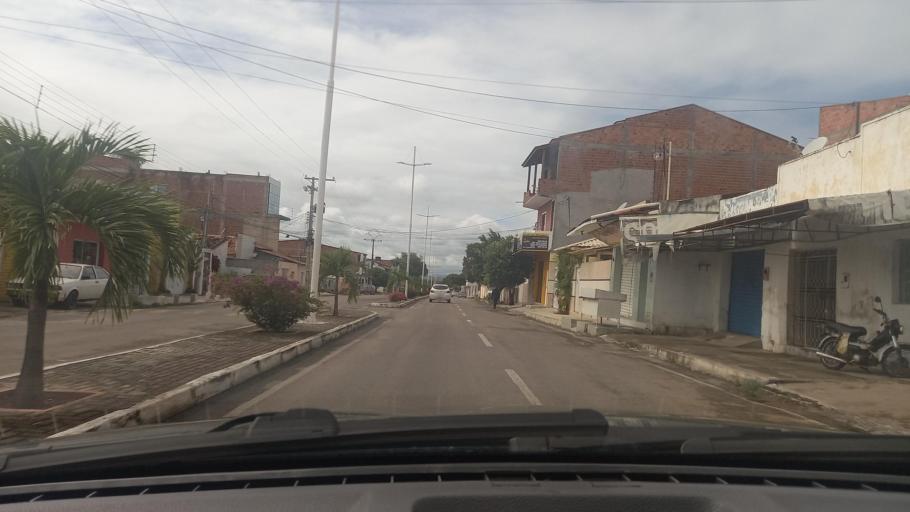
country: BR
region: Bahia
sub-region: Paulo Afonso
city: Paulo Afonso
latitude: -9.4401
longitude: -38.2135
